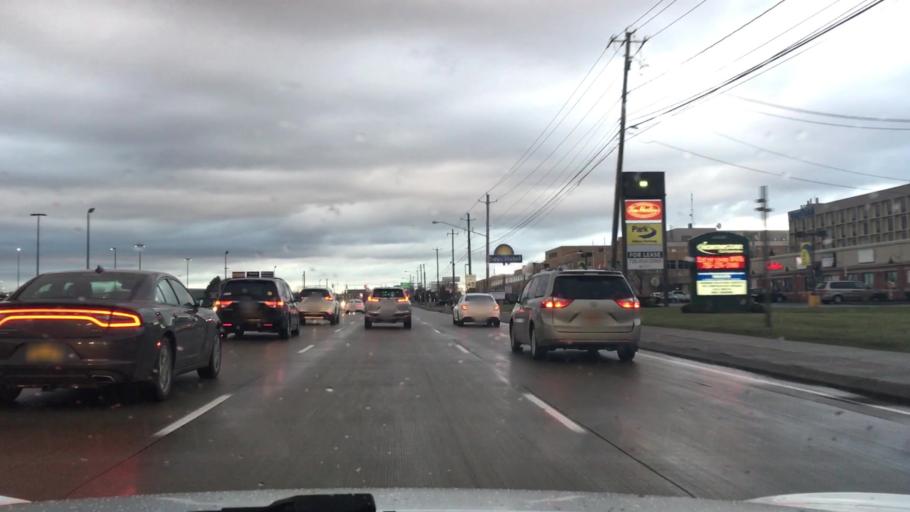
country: US
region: New York
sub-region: Erie County
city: Williamsville
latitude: 42.9327
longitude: -78.7273
